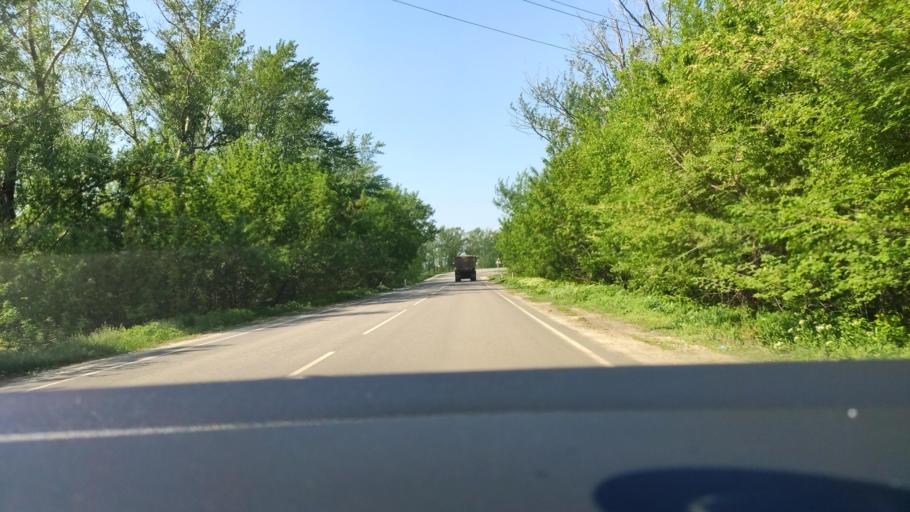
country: RU
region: Voronezj
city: Maslovka
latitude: 51.5315
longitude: 39.3135
